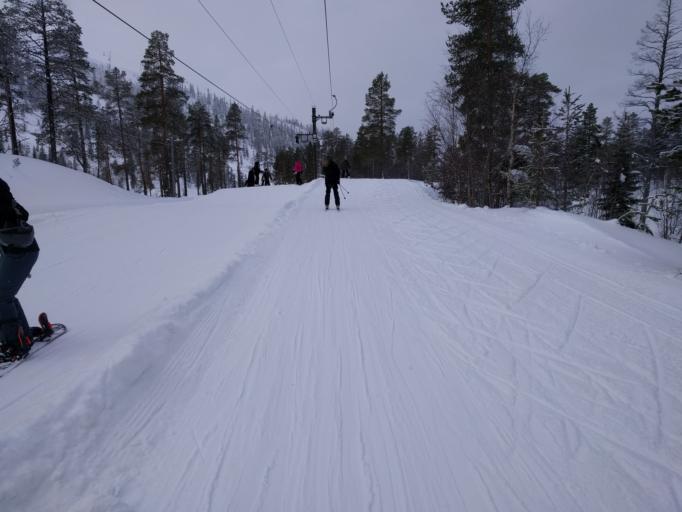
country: NO
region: Hedmark
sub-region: Trysil
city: Innbygda
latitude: 61.1734
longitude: 12.9833
